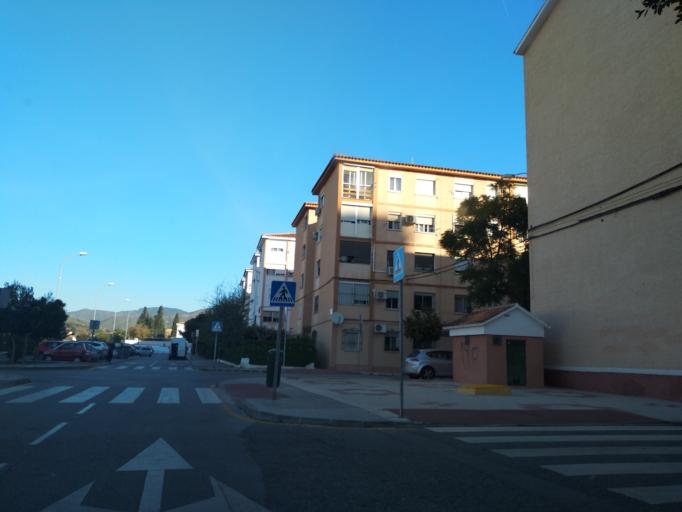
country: ES
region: Andalusia
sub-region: Provincia de Malaga
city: Malaga
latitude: 36.7452
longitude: -4.4242
